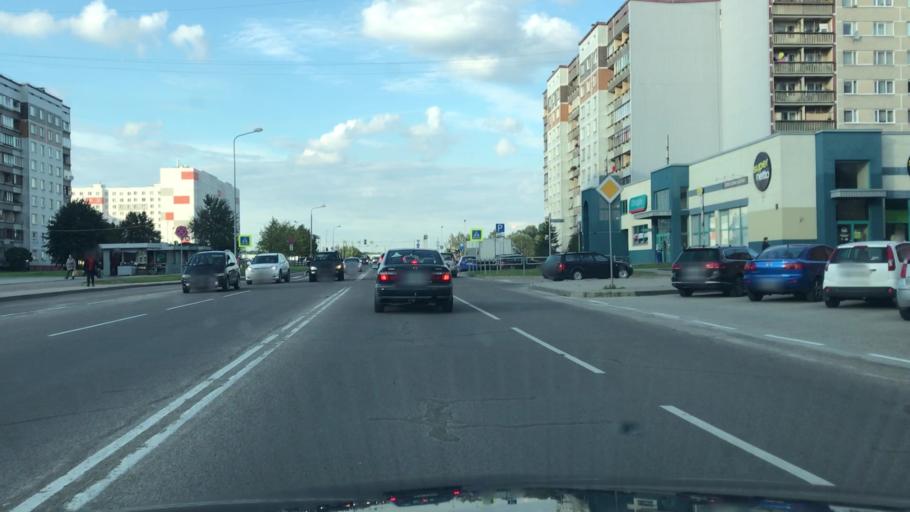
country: LV
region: Stopini
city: Ulbroka
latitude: 56.9431
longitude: 24.2168
